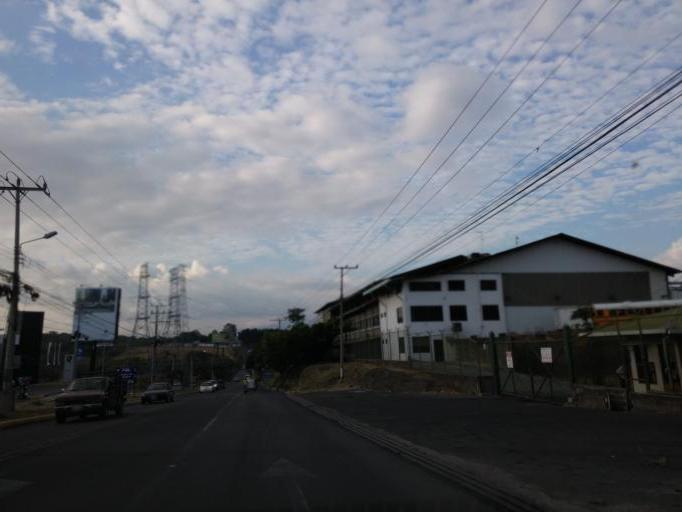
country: CR
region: Heredia
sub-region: Canton de Belen
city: San Antonio
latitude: 9.9629
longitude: -84.1980
